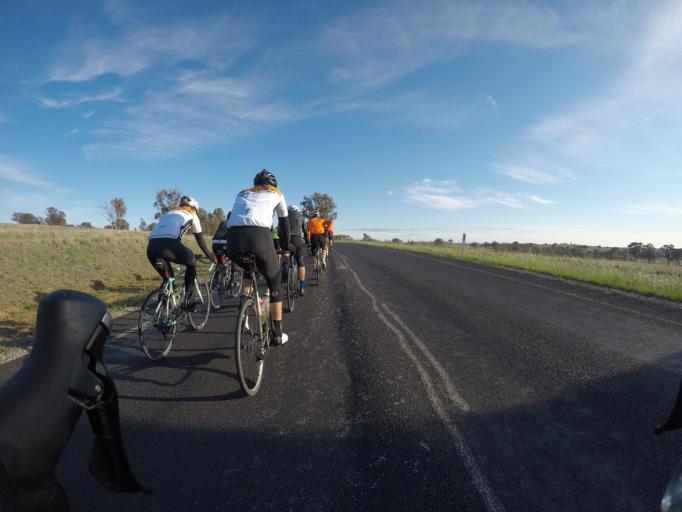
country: AU
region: New South Wales
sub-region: Cabonne
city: Molong
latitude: -32.9692
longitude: 148.7841
